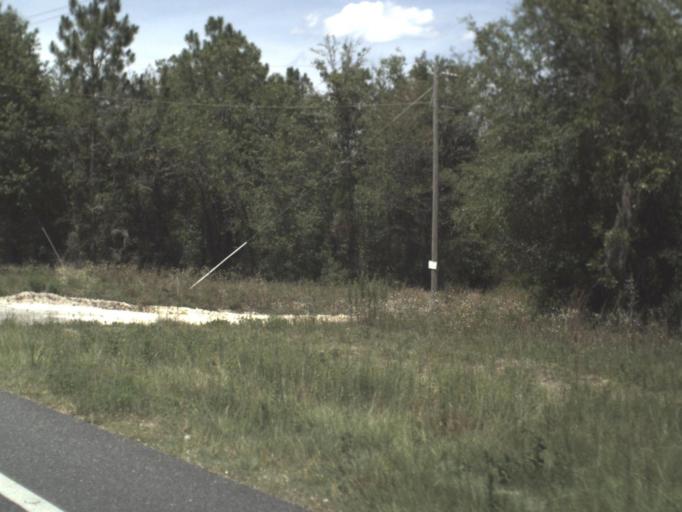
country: US
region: Florida
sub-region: Gilchrist County
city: Trenton
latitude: 29.8035
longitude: -82.8670
